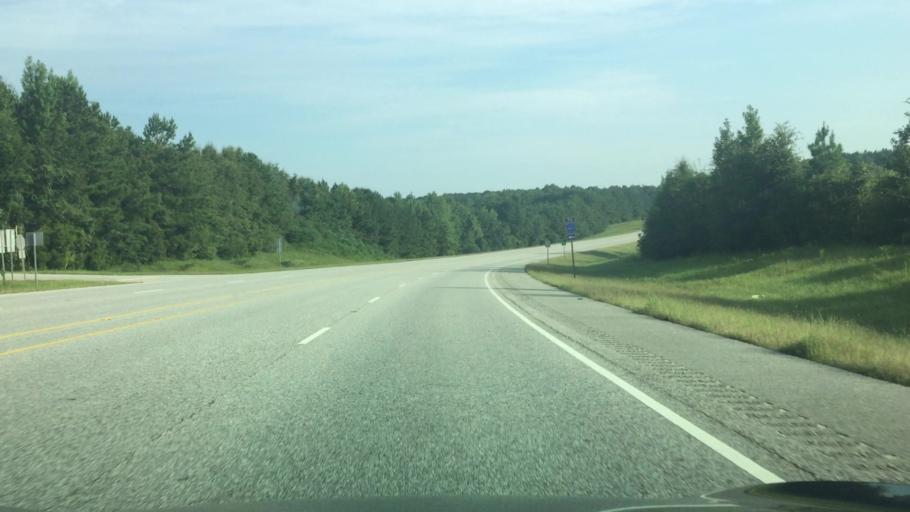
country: US
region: Alabama
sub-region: Butler County
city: Georgiana
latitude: 31.5055
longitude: -86.7010
